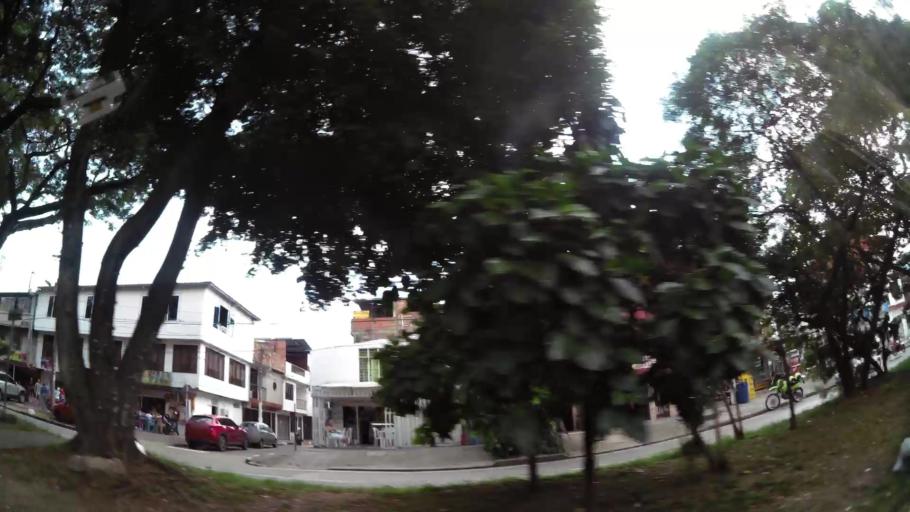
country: CO
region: Valle del Cauca
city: Cali
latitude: 3.4126
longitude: -76.5267
